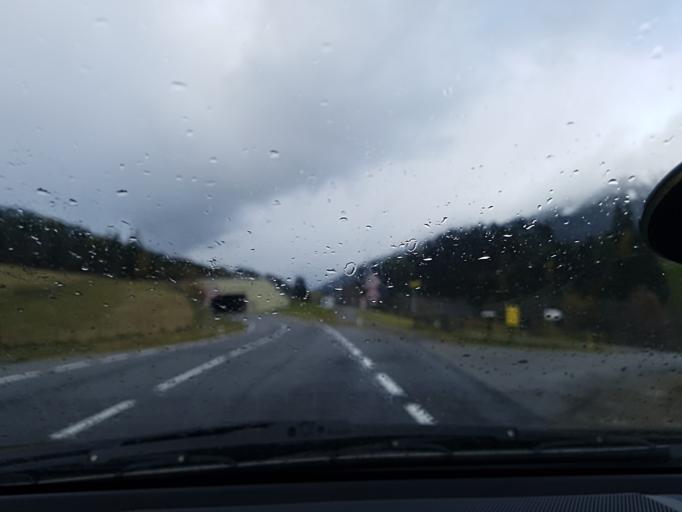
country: AT
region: Styria
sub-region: Politischer Bezirk Murtal
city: Sankt Johann am Tauern
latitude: 47.3716
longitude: 14.4613
